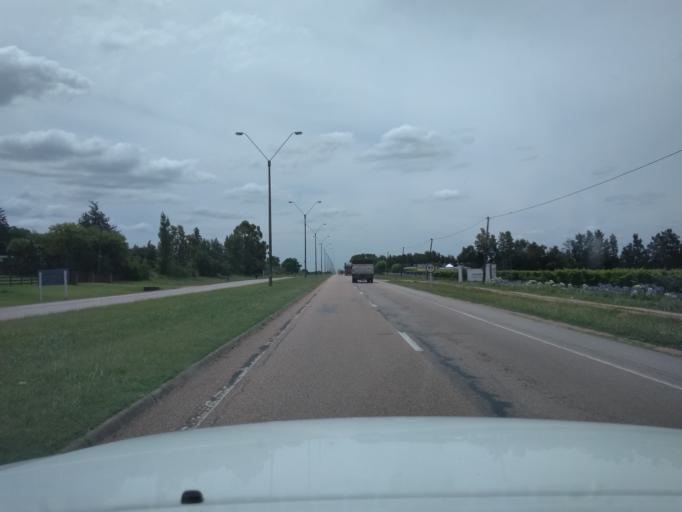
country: UY
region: Canelones
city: Joanico
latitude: -34.5910
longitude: -56.2627
